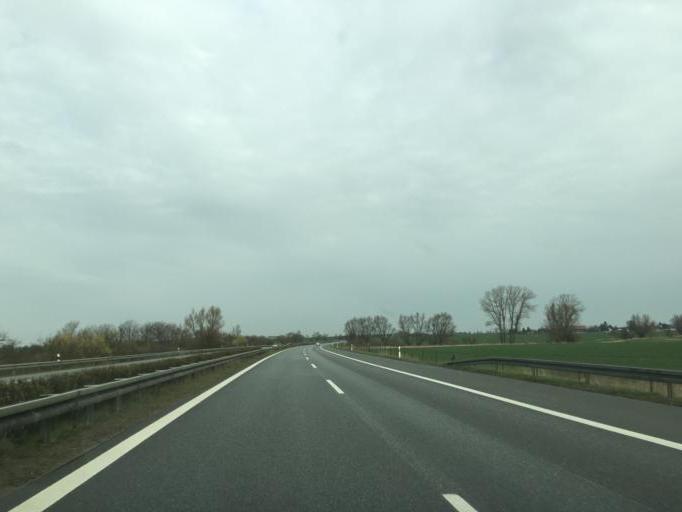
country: DE
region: Mecklenburg-Vorpommern
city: Muhl Rosin
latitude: 53.8588
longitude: 12.2625
